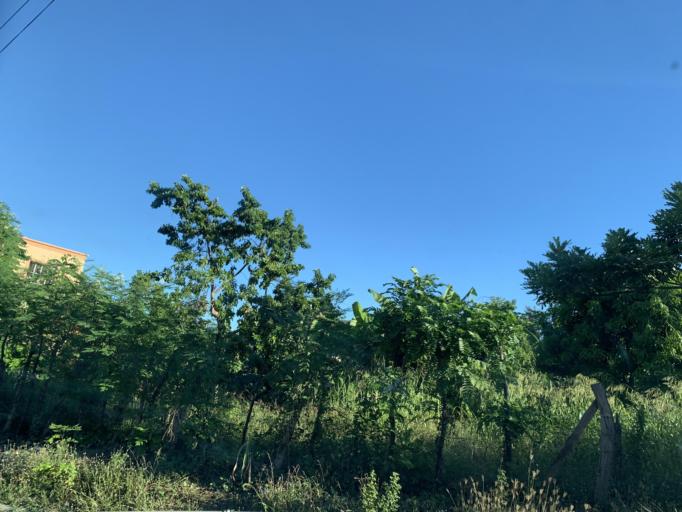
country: DO
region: Puerto Plata
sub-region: Puerto Plata
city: Puerto Plata
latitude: 19.7897
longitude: -70.6950
